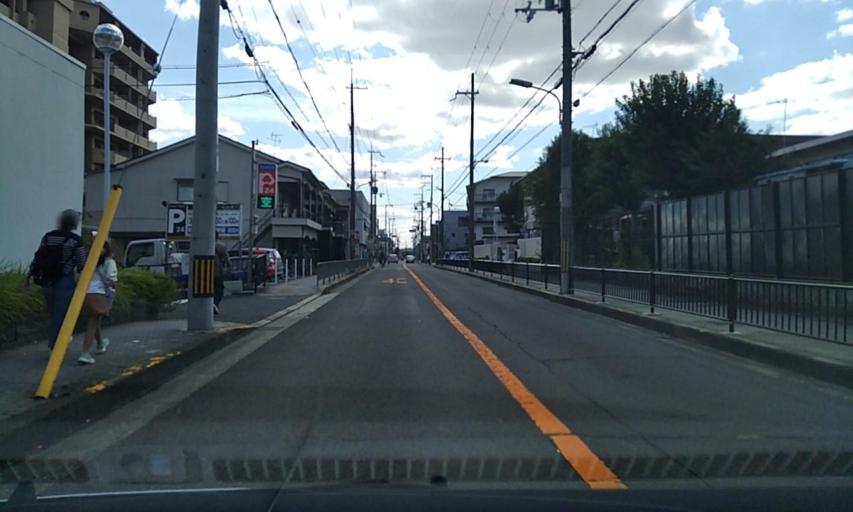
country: JP
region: Osaka
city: Ibaraki
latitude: 34.8251
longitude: 135.5659
